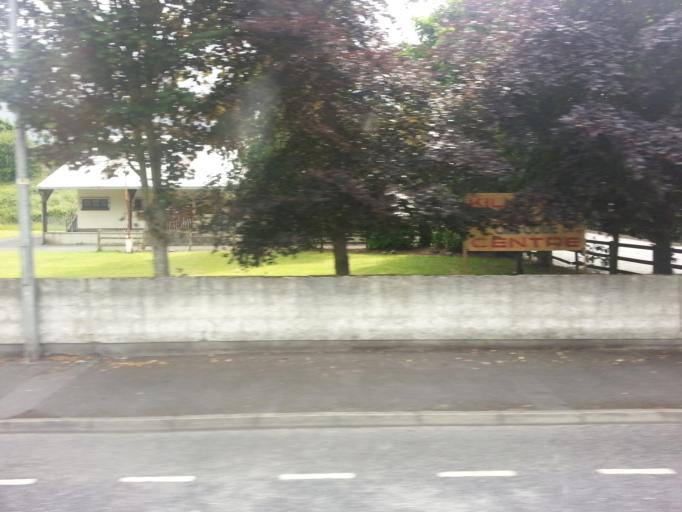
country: IE
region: Leinster
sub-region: Kilkenny
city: Kilkenny
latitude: 52.6440
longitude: -7.2367
